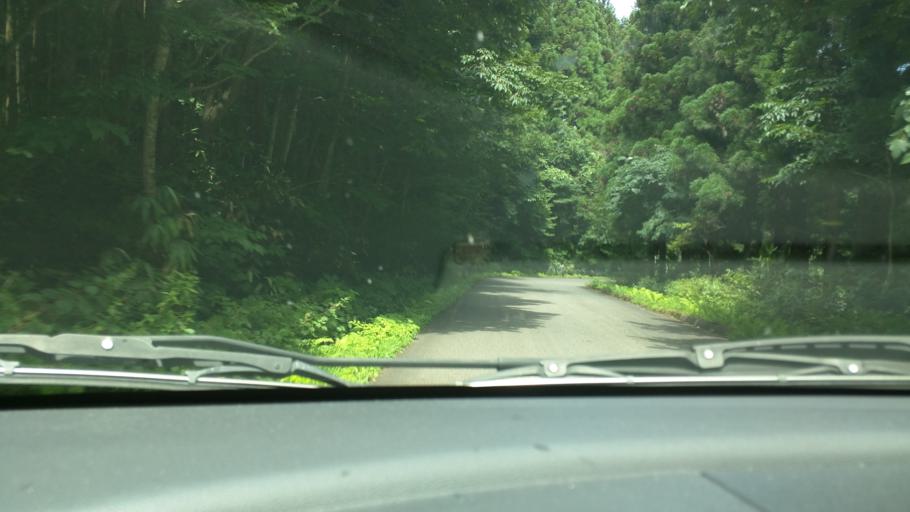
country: JP
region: Fukushima
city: Inawashiro
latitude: 37.3446
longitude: 140.0574
